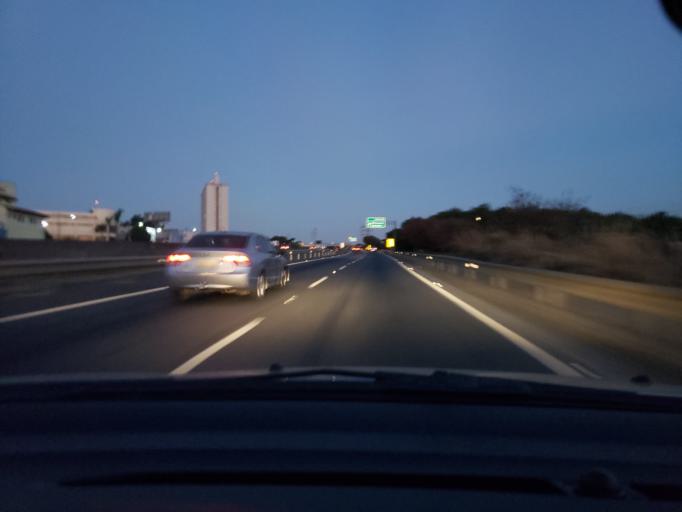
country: BR
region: Sao Paulo
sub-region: Campinas
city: Campinas
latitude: -22.9162
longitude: -47.0975
